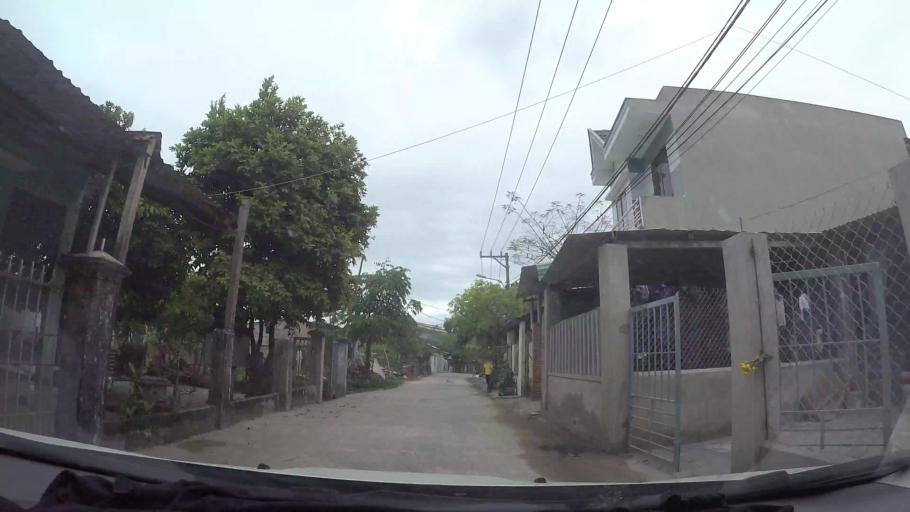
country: VN
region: Da Nang
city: Lien Chieu
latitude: 16.0891
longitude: 108.1022
